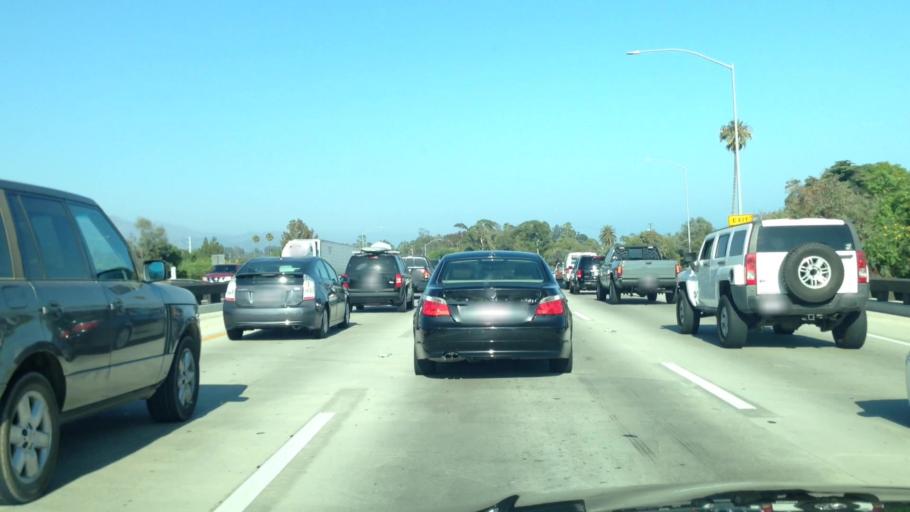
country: US
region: California
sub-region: Santa Barbara County
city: Santa Barbara
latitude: 34.4206
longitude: -119.6759
